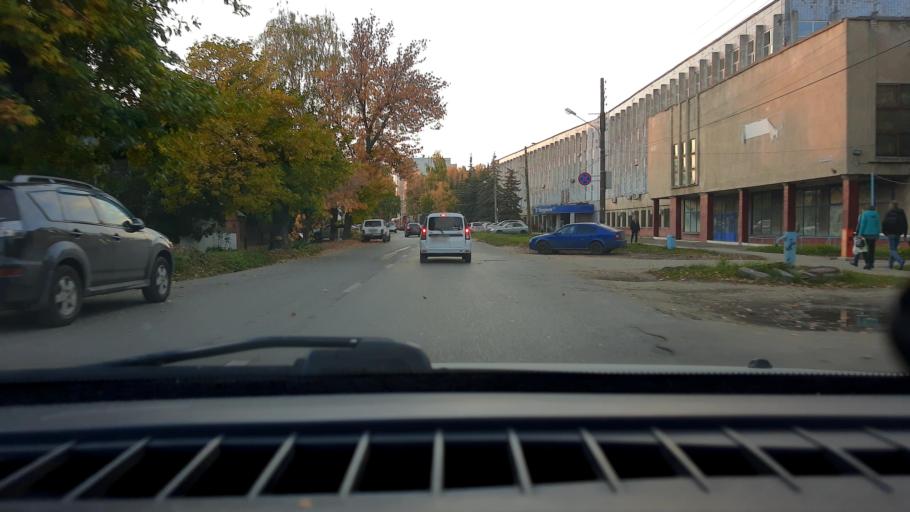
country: RU
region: Nizjnij Novgorod
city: Neklyudovo
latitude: 56.3599
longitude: 43.8687
